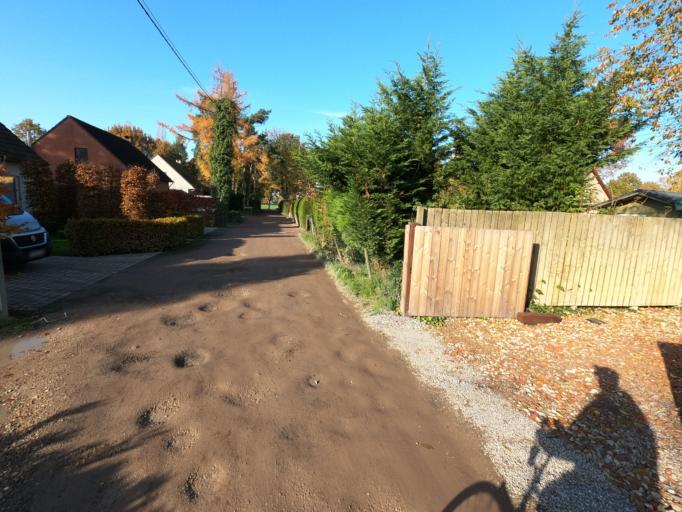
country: BE
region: Flanders
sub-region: Provincie Antwerpen
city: Wuustwezel
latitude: 51.3443
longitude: 4.5457
